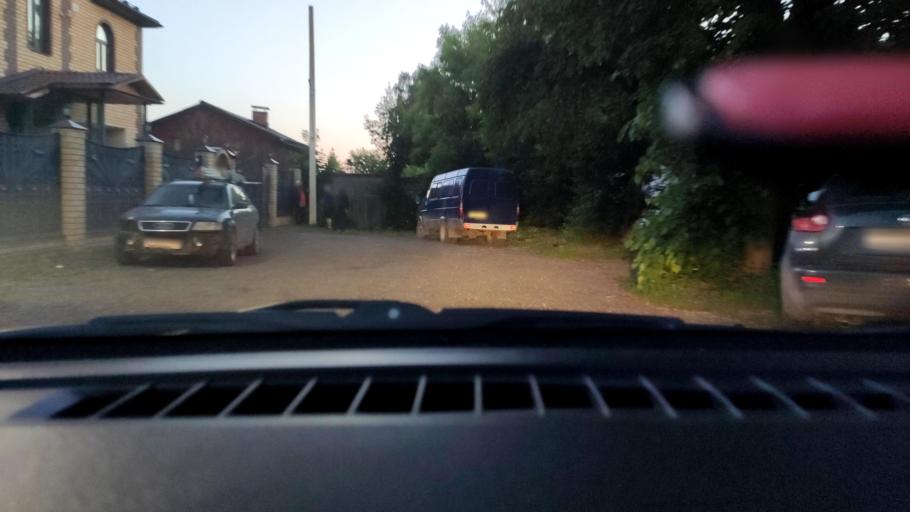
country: RU
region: Perm
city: Kondratovo
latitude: 57.9659
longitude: 56.1341
